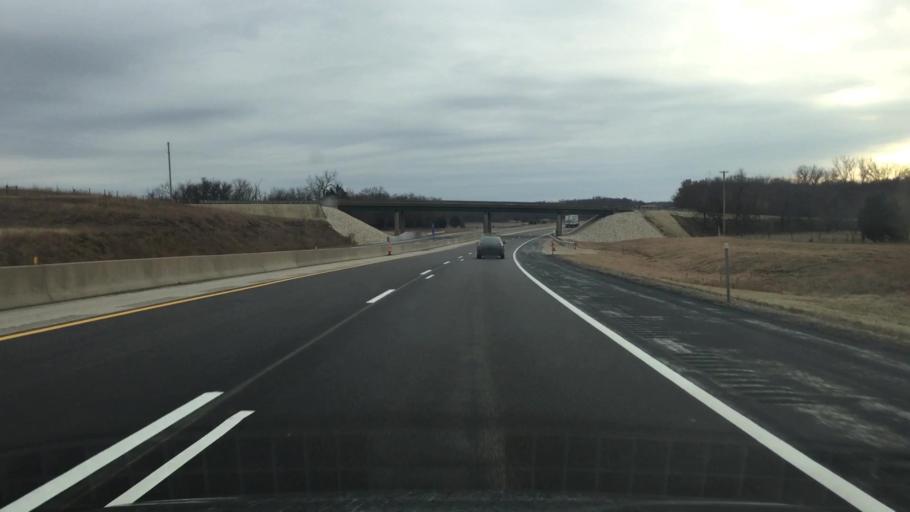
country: US
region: Kansas
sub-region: Osage County
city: Osage City
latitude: 38.6241
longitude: -96.0462
